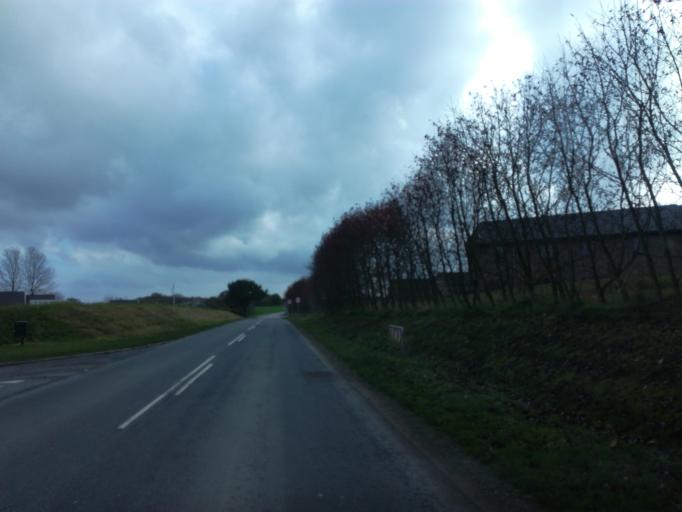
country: DK
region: South Denmark
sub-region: Vejle Kommune
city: Borkop
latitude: 55.6346
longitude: 9.6439
